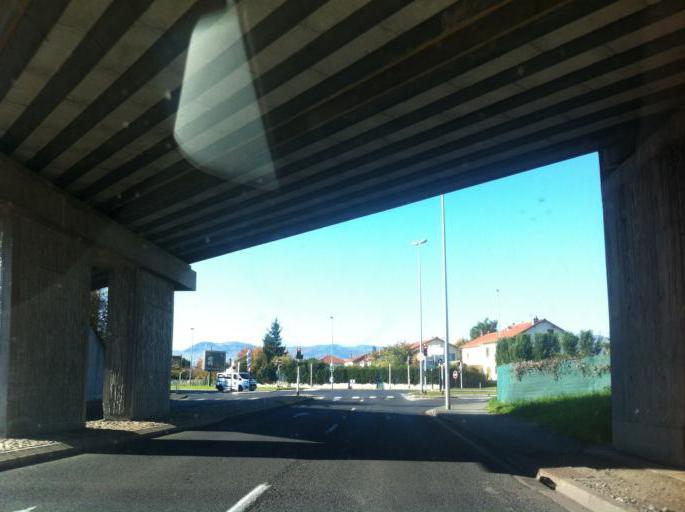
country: FR
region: Auvergne
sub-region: Departement du Puy-de-Dome
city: Aulnat
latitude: 45.7981
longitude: 3.1541
